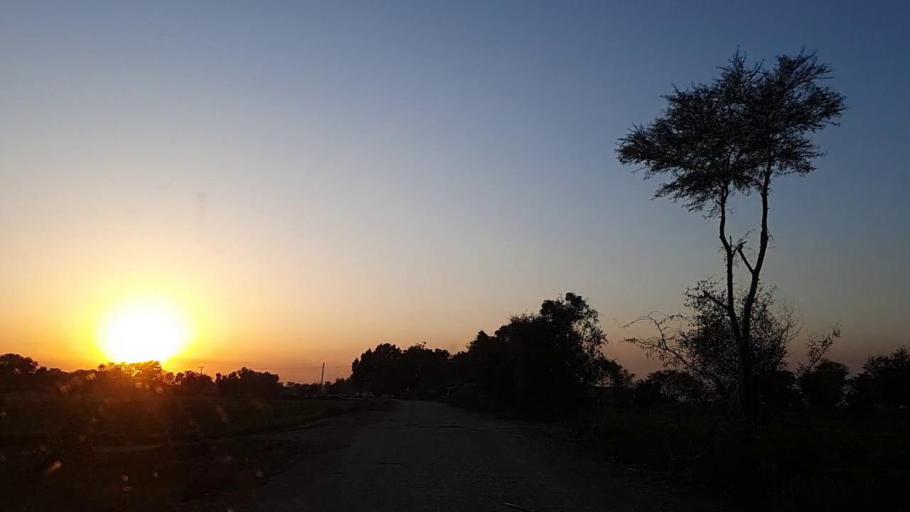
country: PK
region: Sindh
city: Daur
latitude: 26.3504
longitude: 68.3112
